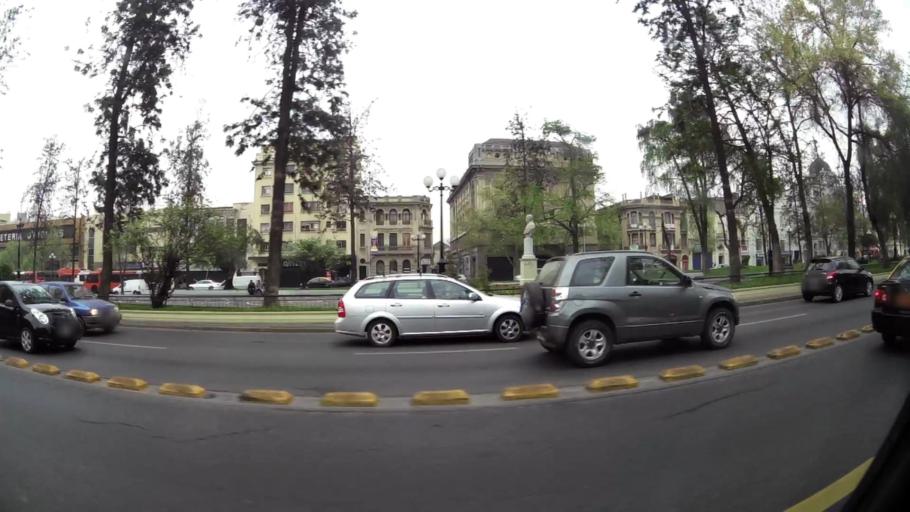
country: CL
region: Santiago Metropolitan
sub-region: Provincia de Santiago
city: Santiago
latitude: -33.4476
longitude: -70.6658
